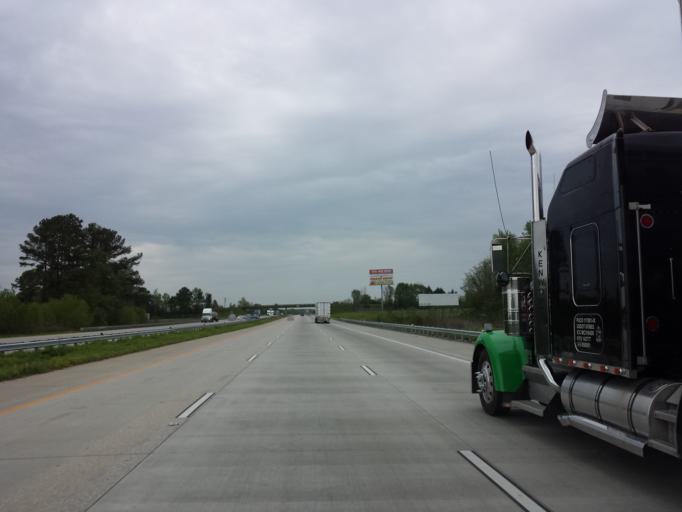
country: US
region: Georgia
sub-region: Dooly County
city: Unadilla
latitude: 32.2866
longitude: -83.7576
